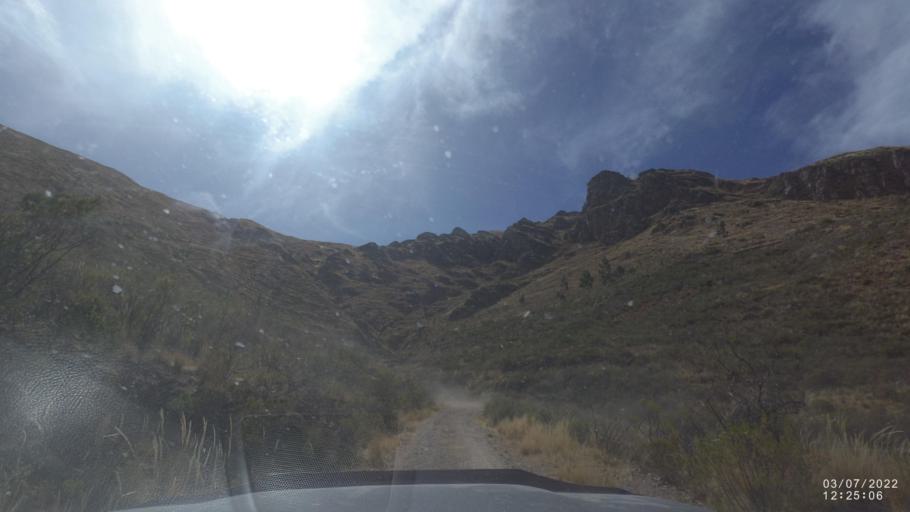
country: BO
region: Cochabamba
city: Irpa Irpa
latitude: -17.8106
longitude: -66.6167
